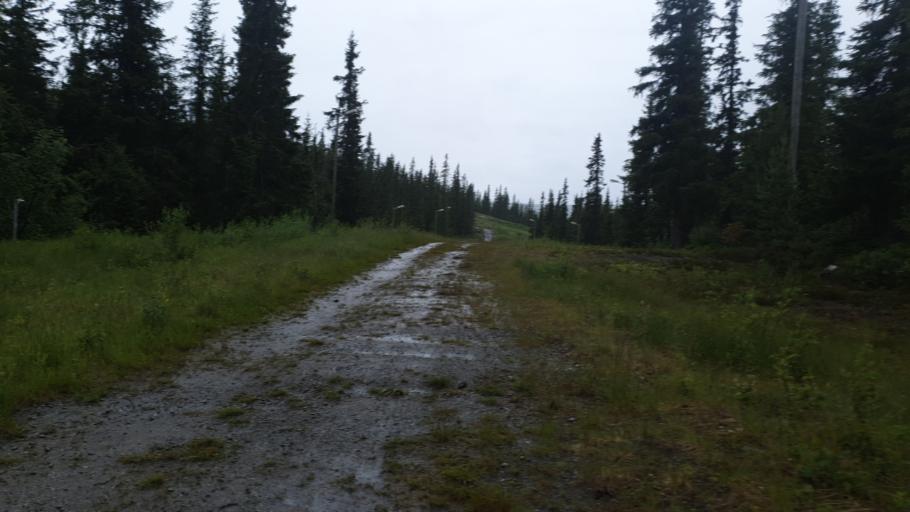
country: NO
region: Oppland
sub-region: Vestre Slidre
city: Slidre
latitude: 61.2330
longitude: 8.9143
